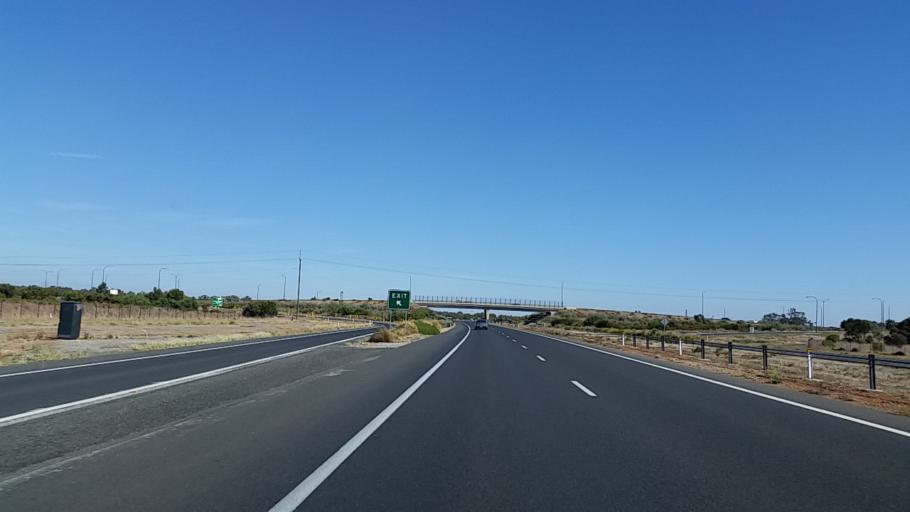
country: AU
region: South Australia
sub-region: Playford
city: Angle Vale
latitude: -34.6600
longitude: 138.6565
